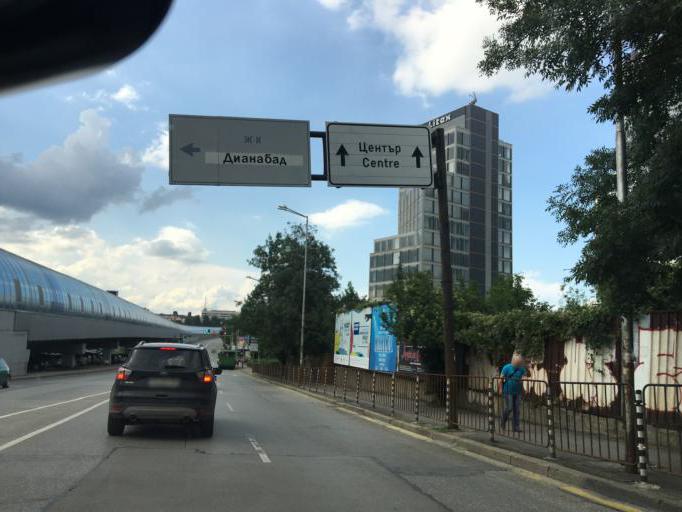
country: BG
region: Sofia-Capital
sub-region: Stolichna Obshtina
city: Sofia
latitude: 42.6644
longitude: 23.3564
